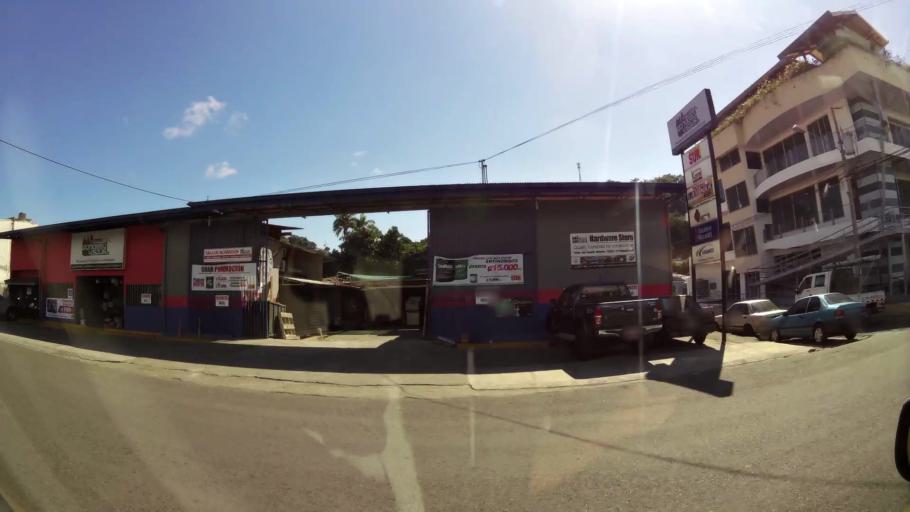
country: CR
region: Puntarenas
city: Quepos
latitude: 9.4316
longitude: -84.1618
